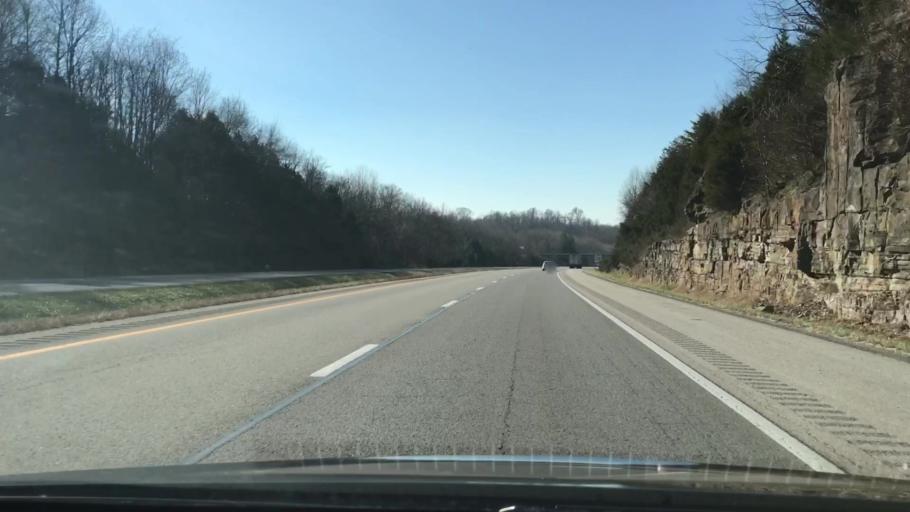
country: US
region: Kentucky
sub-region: Barren County
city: Glasgow
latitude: 36.9775
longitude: -85.9070
